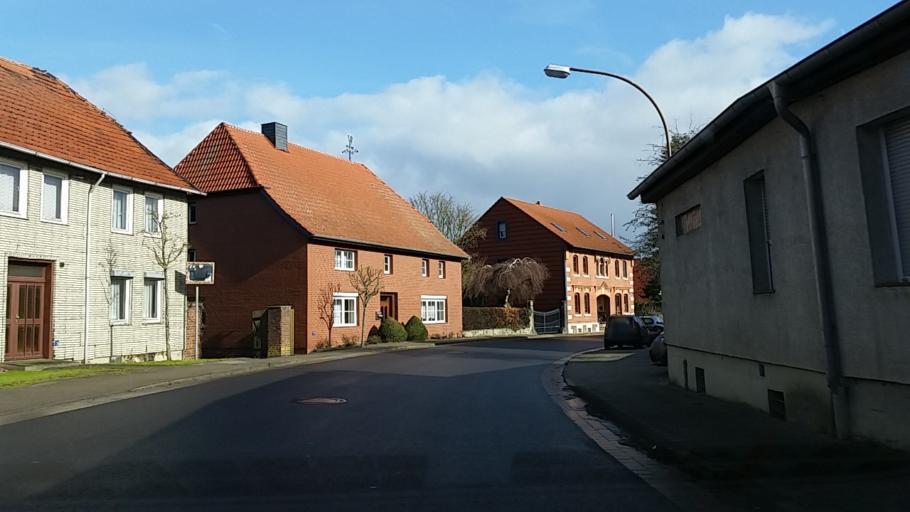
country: DE
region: Lower Saxony
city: Gross Twulpstedt
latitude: 52.3855
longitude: 10.9205
